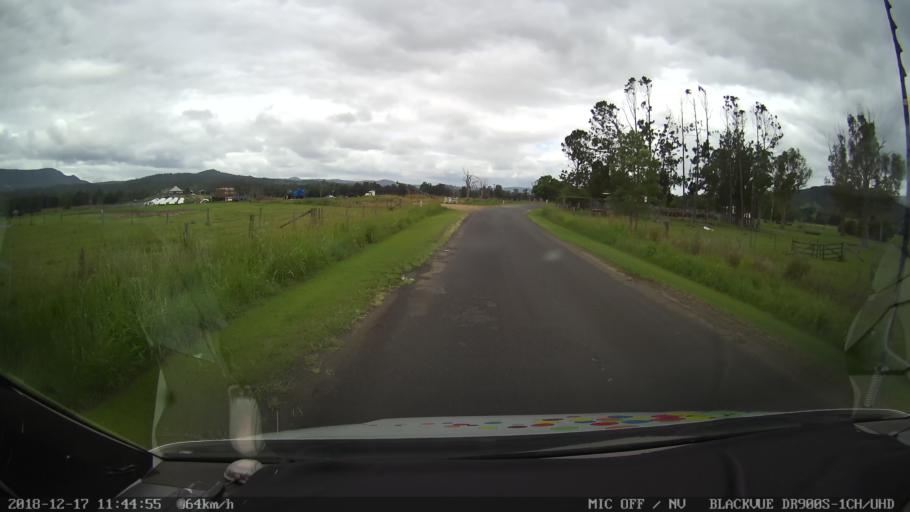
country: AU
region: New South Wales
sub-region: Kyogle
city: Kyogle
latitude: -28.6487
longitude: 152.5948
